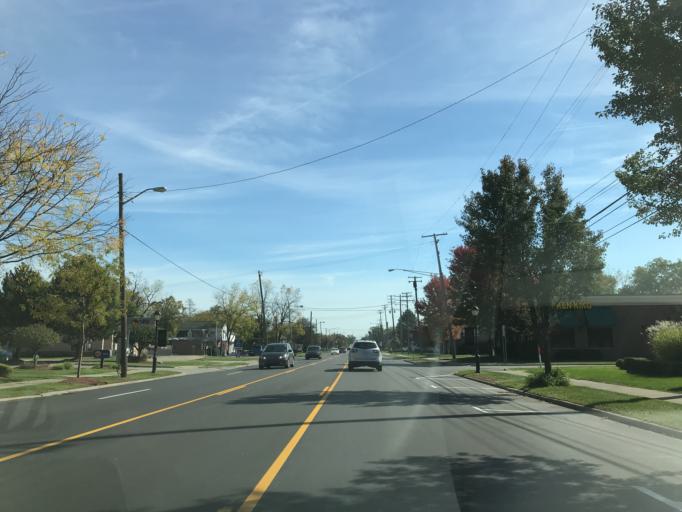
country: US
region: Michigan
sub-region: Oakland County
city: Farmington
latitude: 42.4623
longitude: -83.3703
